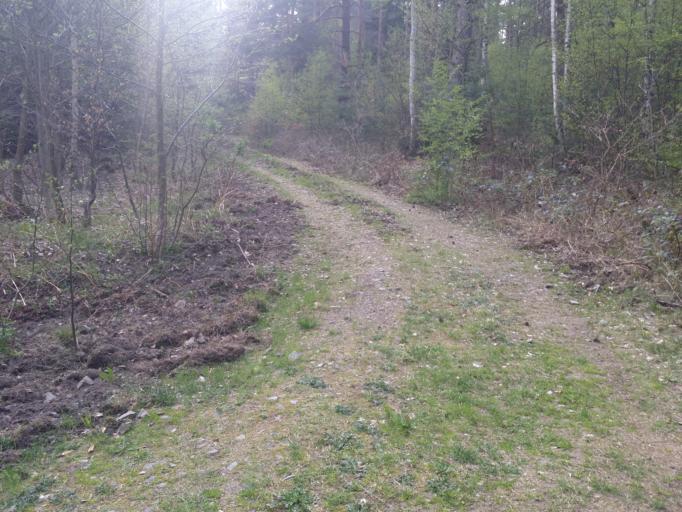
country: DE
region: Saxony-Anhalt
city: Bad Suderode
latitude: 51.7182
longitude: 11.0958
